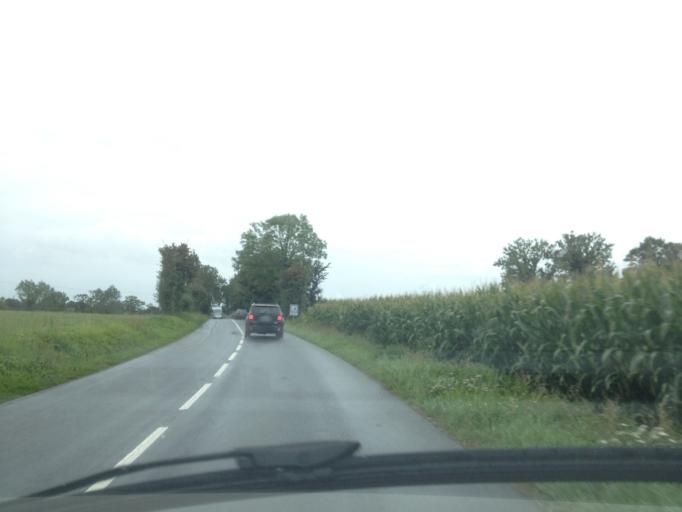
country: FR
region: Lower Normandy
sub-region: Departement du Calvados
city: Saint-Vigor-le-Grand
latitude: 49.3011
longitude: -0.6845
